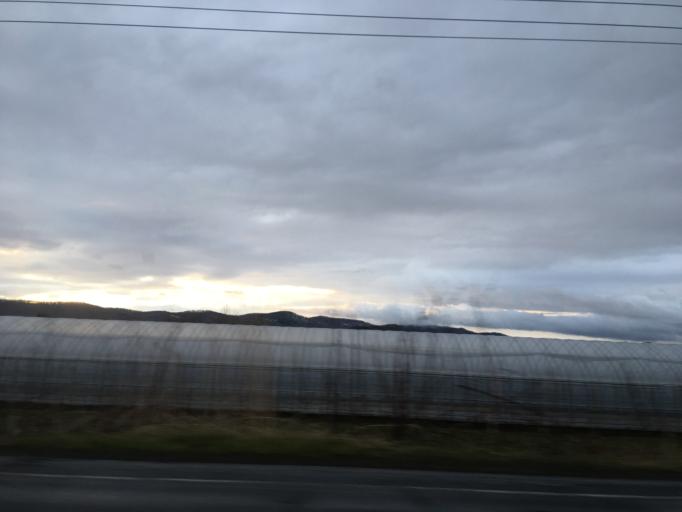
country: JP
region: Hokkaido
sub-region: Asahikawa-shi
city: Asahikawa
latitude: 43.8849
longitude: 142.4968
